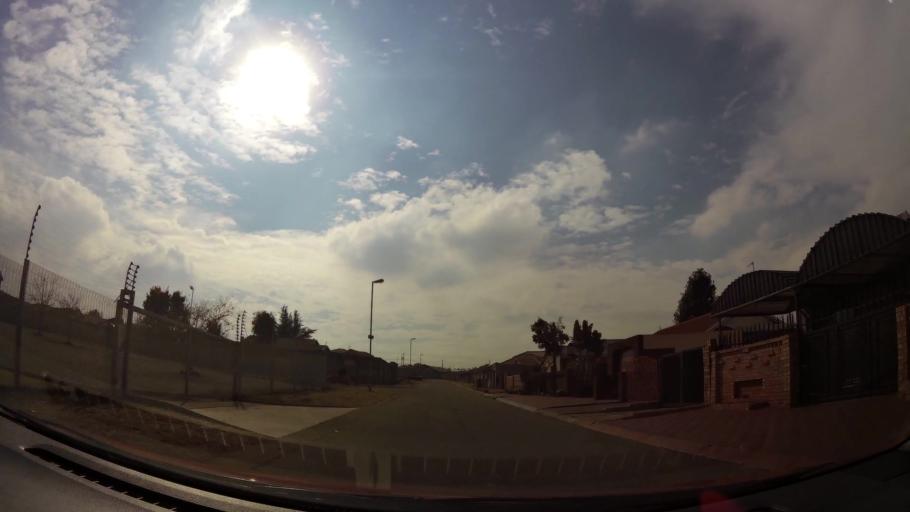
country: ZA
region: Gauteng
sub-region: City of Johannesburg Metropolitan Municipality
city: Soweto
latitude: -26.2640
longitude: 27.8270
